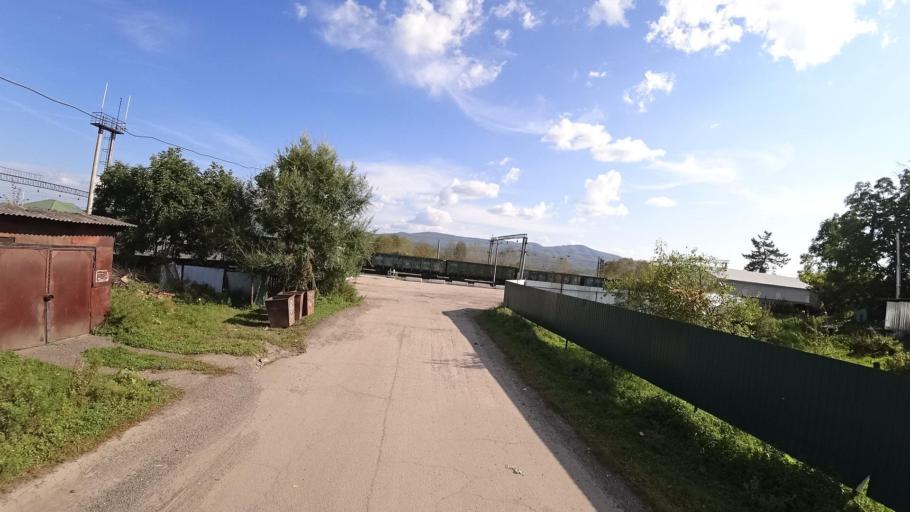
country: RU
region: Jewish Autonomous Oblast
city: Birakan
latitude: 48.9930
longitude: 131.7214
